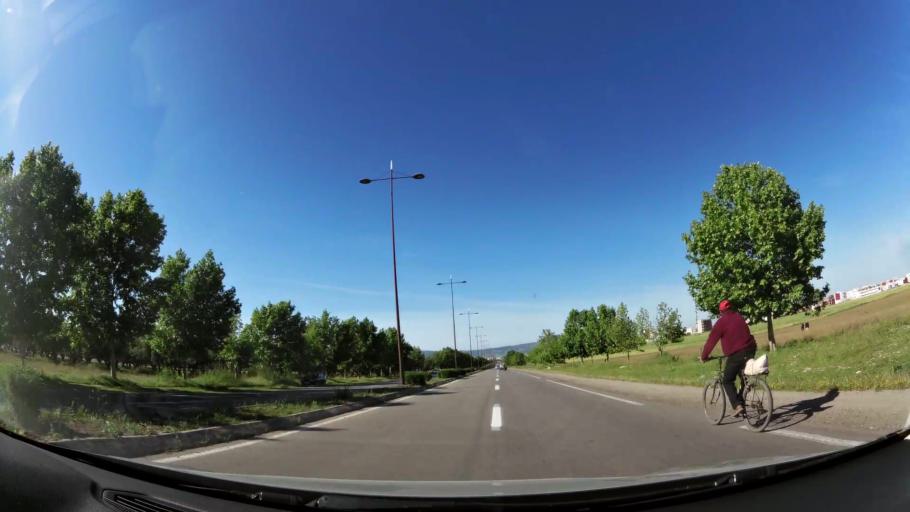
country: MA
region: Fes-Boulemane
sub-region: Fes
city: Fes
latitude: 33.9995
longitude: -5.0243
